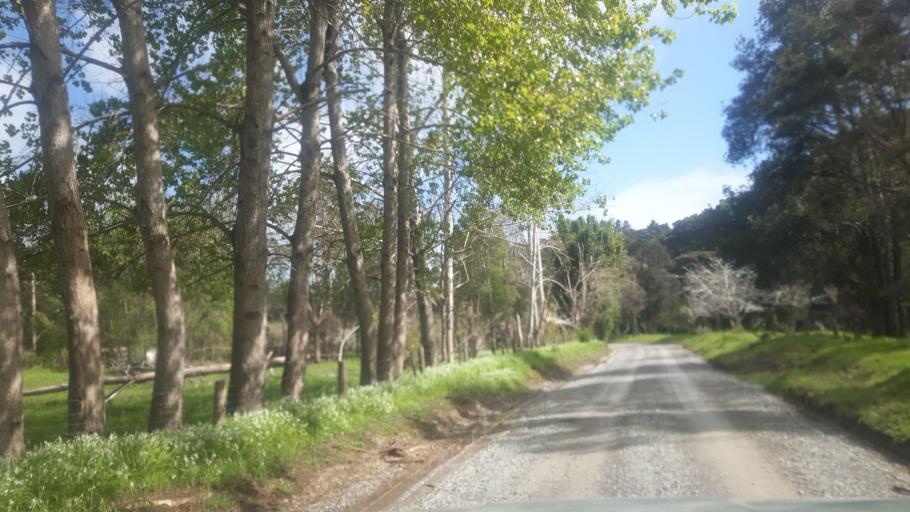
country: NZ
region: Northland
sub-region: Far North District
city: Taipa
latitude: -35.1136
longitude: 173.4307
